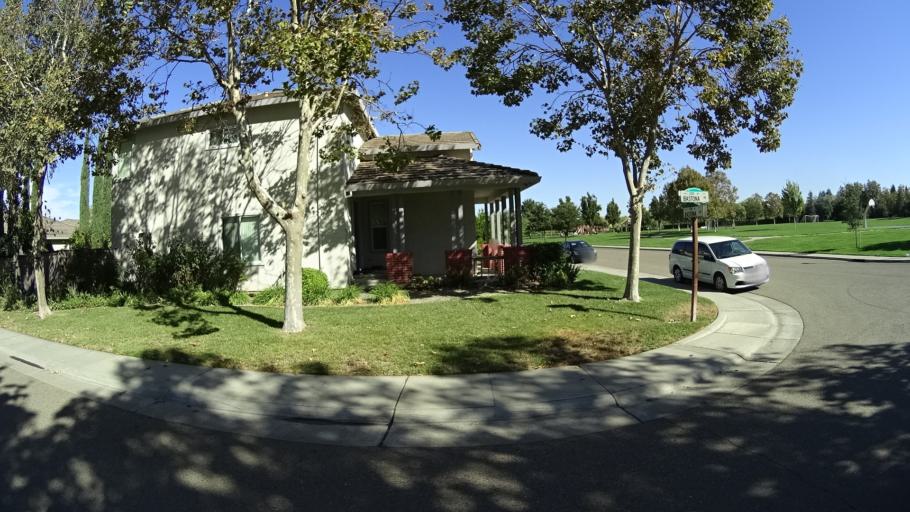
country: US
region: California
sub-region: Sacramento County
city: Laguna
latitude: 38.4198
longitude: -121.4833
